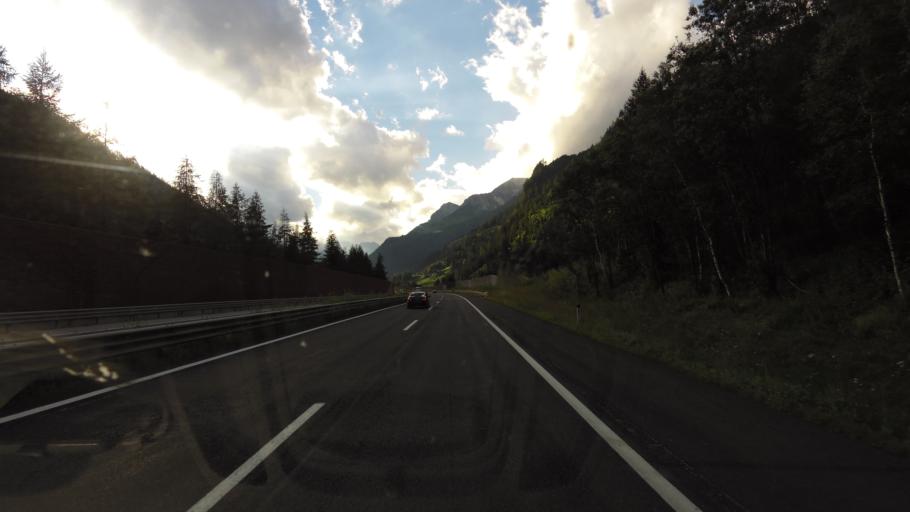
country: AT
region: Salzburg
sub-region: Politischer Bezirk Tamsweg
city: Zederhaus
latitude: 47.1439
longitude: 13.5227
